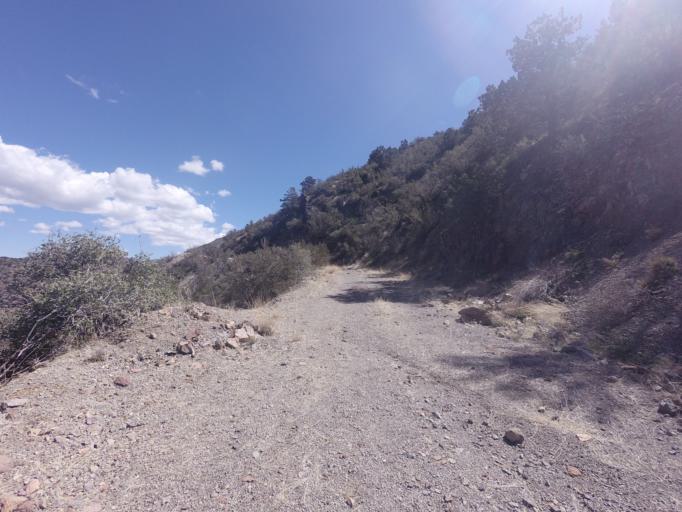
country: US
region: Arizona
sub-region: Gila County
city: Pine
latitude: 34.4028
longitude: -111.6072
